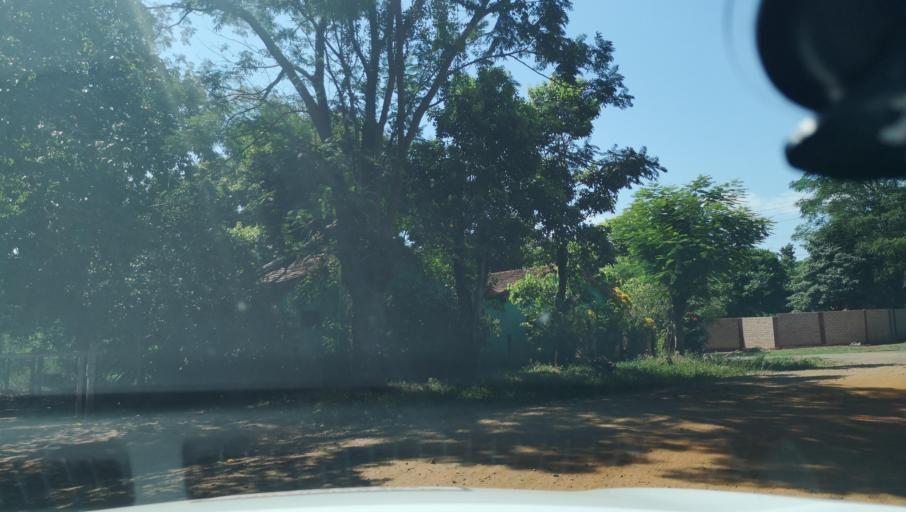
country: PY
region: Itapua
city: Carmen del Parana
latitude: -27.1594
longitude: -56.2473
